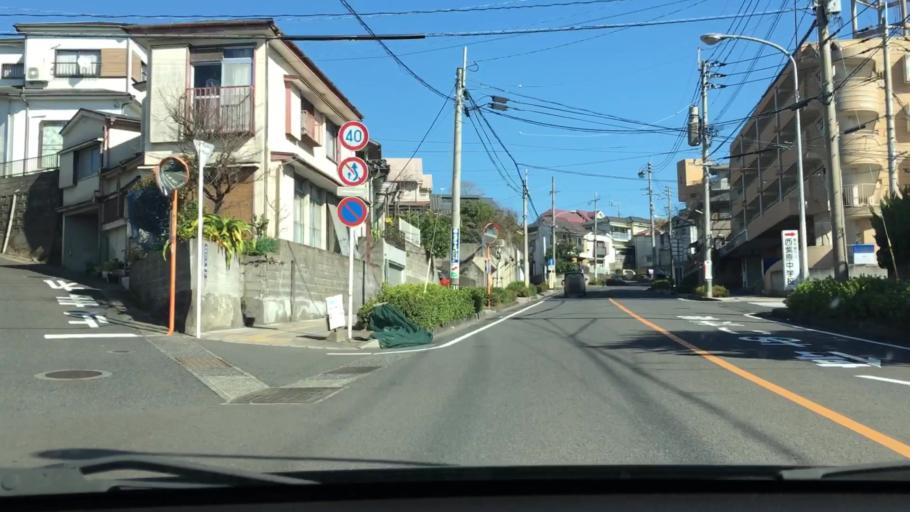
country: JP
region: Kagoshima
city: Kagoshima-shi
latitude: 31.5594
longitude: 130.5267
